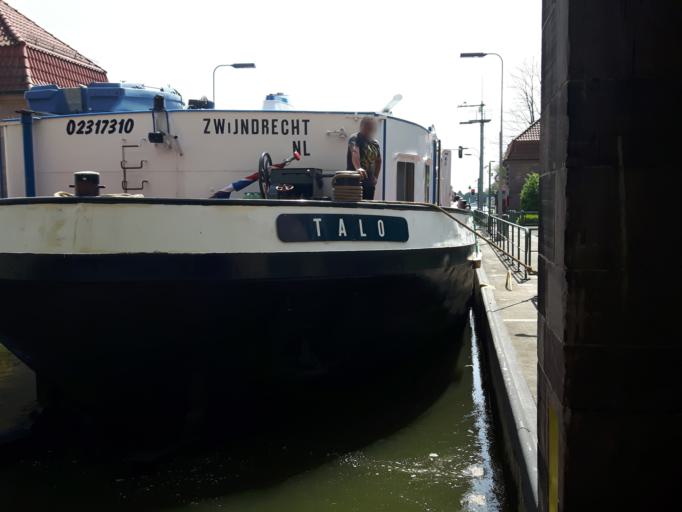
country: DE
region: North Rhine-Westphalia
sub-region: Regierungsbezirk Detmold
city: Minden
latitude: 52.3068
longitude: 8.9195
